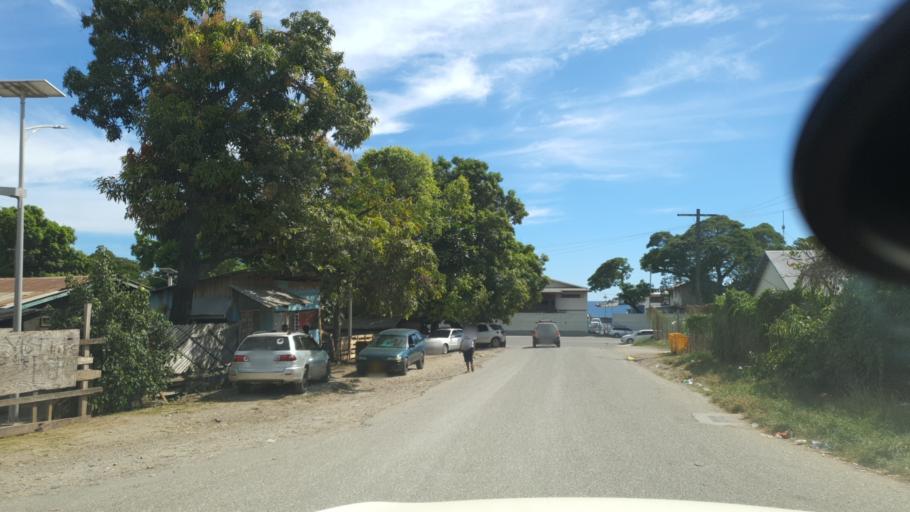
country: SB
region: Guadalcanal
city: Honiara
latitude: -9.4335
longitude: 159.9802
